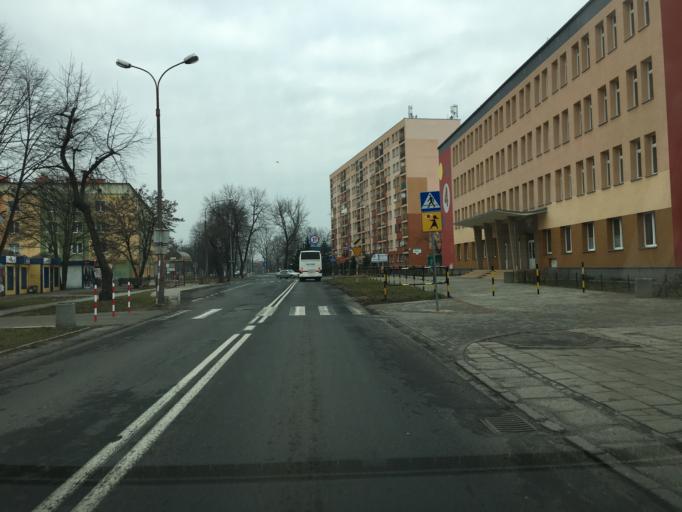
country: PL
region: Opole Voivodeship
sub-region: Powiat kedzierzynsko-kozielski
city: Kedzierzyn-Kozle
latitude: 50.3447
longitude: 18.2159
